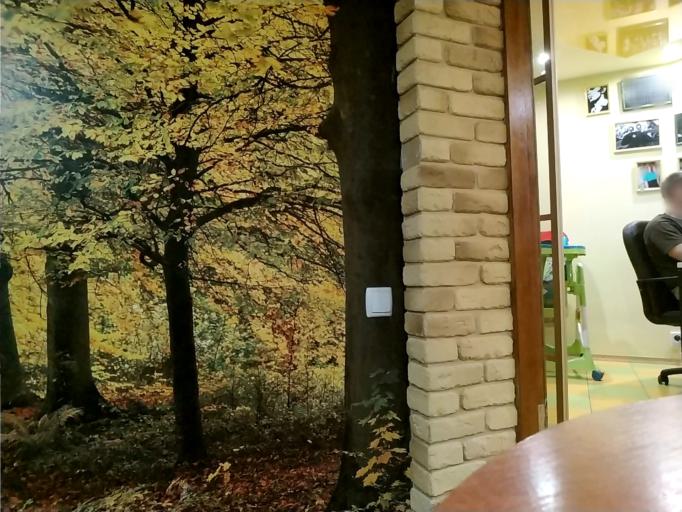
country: RU
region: Tverskaya
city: Zapadnaya Dvina
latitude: 56.3254
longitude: 31.9082
